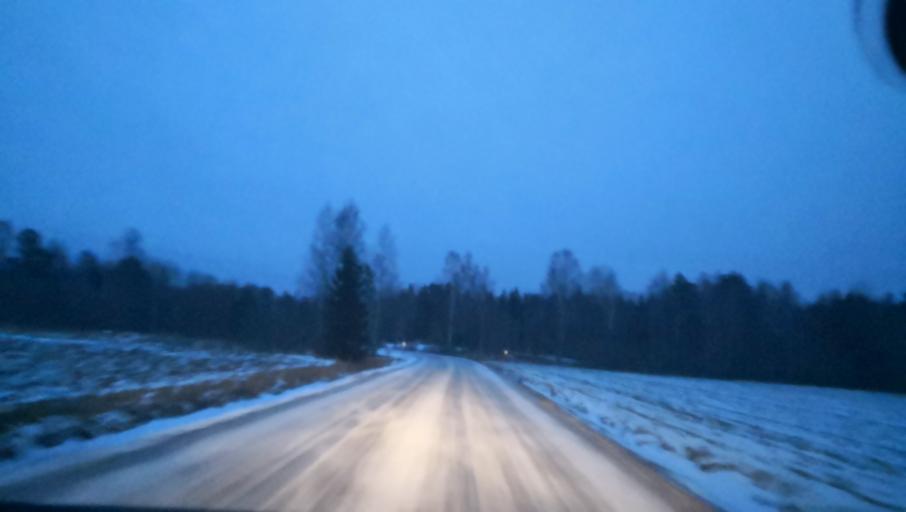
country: SE
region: Uppsala
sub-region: Heby Kommun
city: Tarnsjo
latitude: 60.2435
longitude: 16.6872
